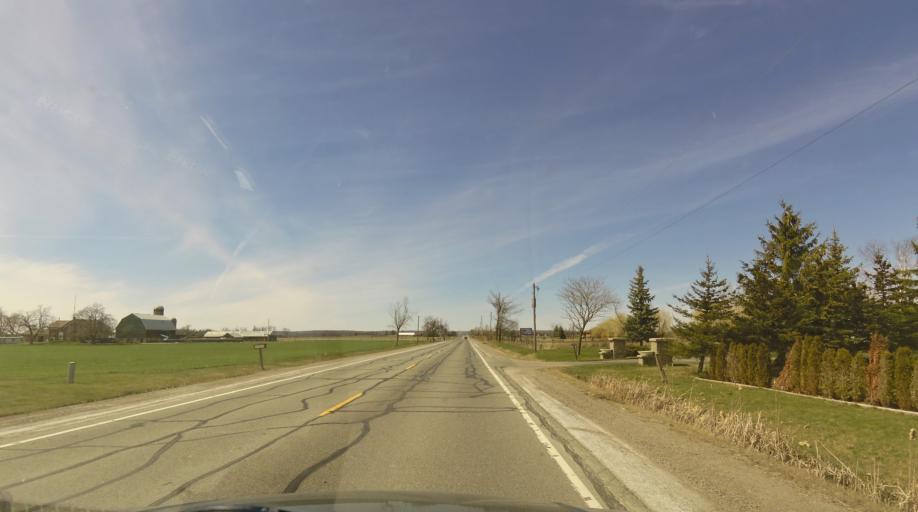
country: CA
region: Ontario
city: Brampton
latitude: 43.7024
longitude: -79.8777
